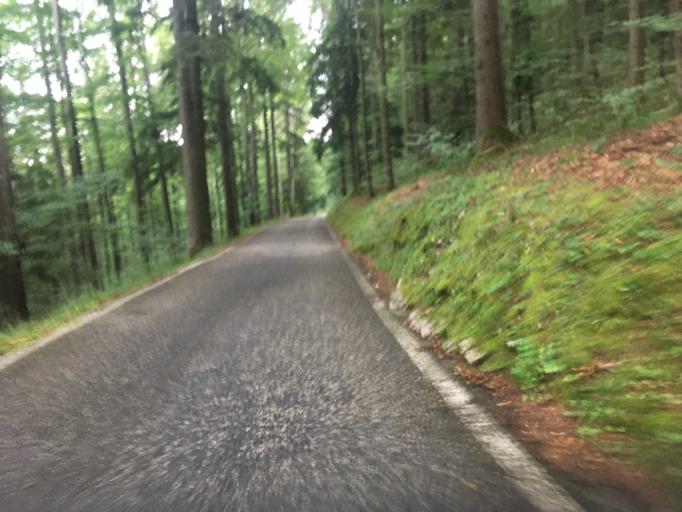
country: CH
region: Solothurn
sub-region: Bezirk Thal
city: Welschenrohr
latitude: 47.2598
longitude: 7.5067
